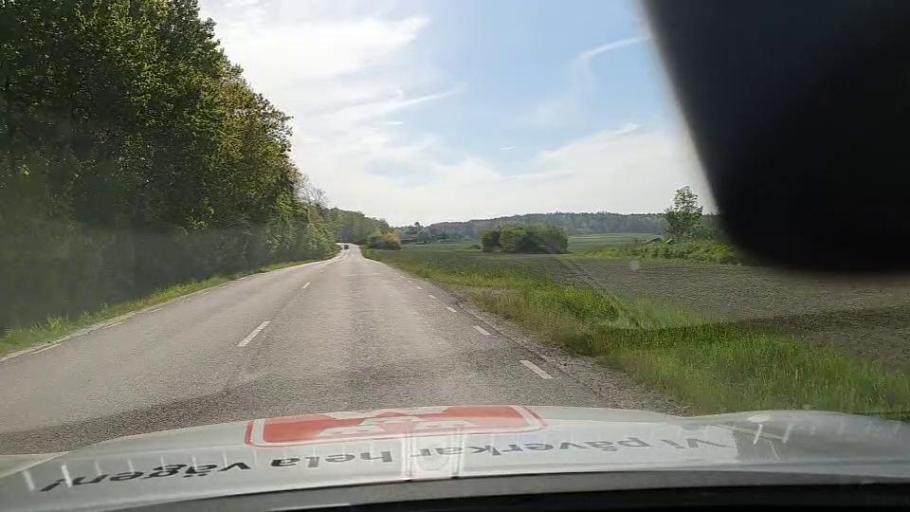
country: SE
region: Soedermanland
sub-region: Eskilstuna Kommun
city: Eskilstuna
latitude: 59.3181
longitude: 16.5797
